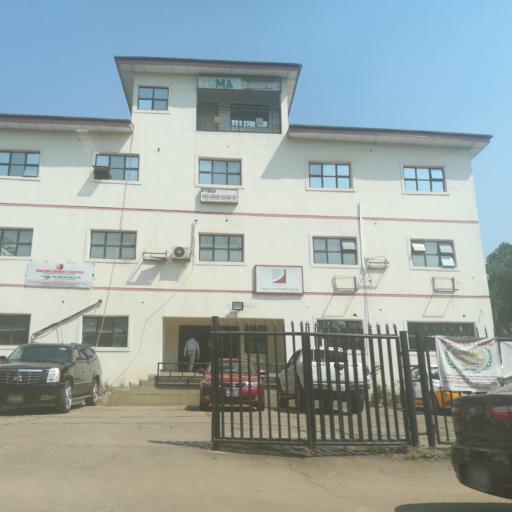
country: NG
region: Abuja Federal Capital Territory
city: Abuja
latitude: 9.0709
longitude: 7.4372
